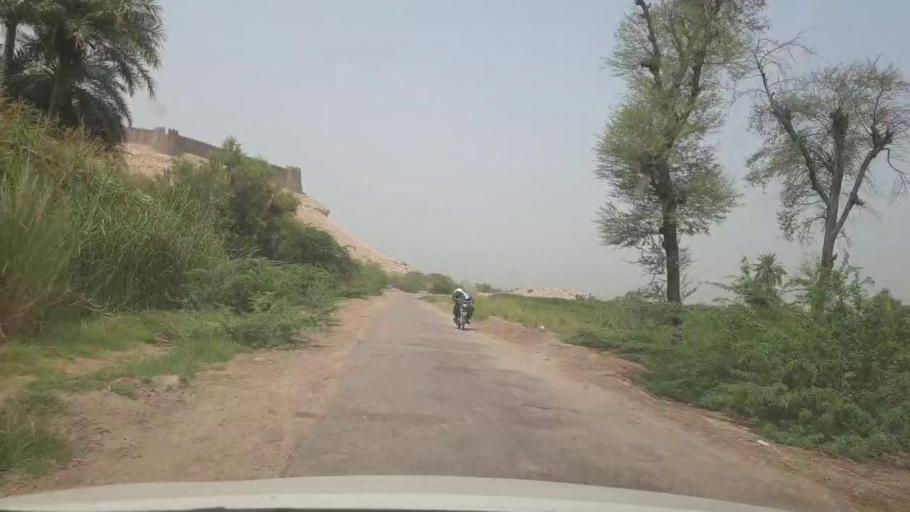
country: PK
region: Sindh
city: Kot Diji
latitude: 27.3489
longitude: 68.7099
